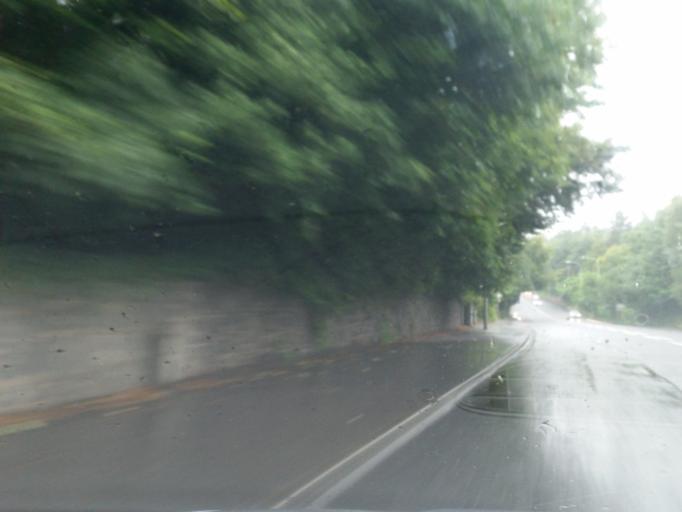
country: GB
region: Northern Ireland
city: Holywood
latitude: 54.6523
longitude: -5.7980
